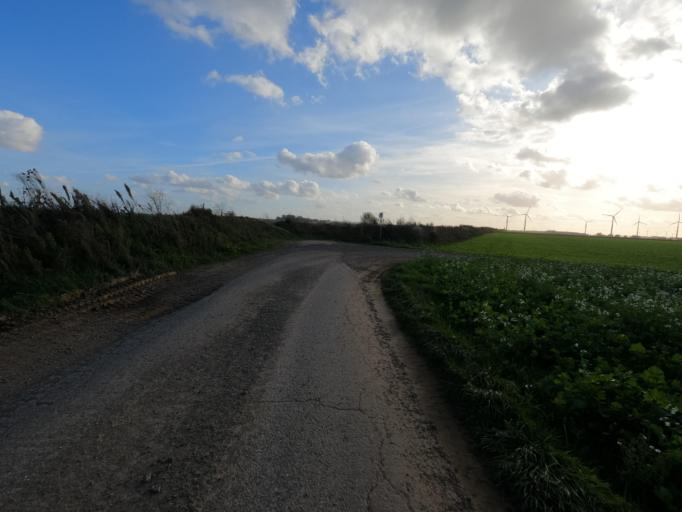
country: DE
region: North Rhine-Westphalia
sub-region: Regierungsbezirk Koln
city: Titz
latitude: 51.0770
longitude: 6.4183
